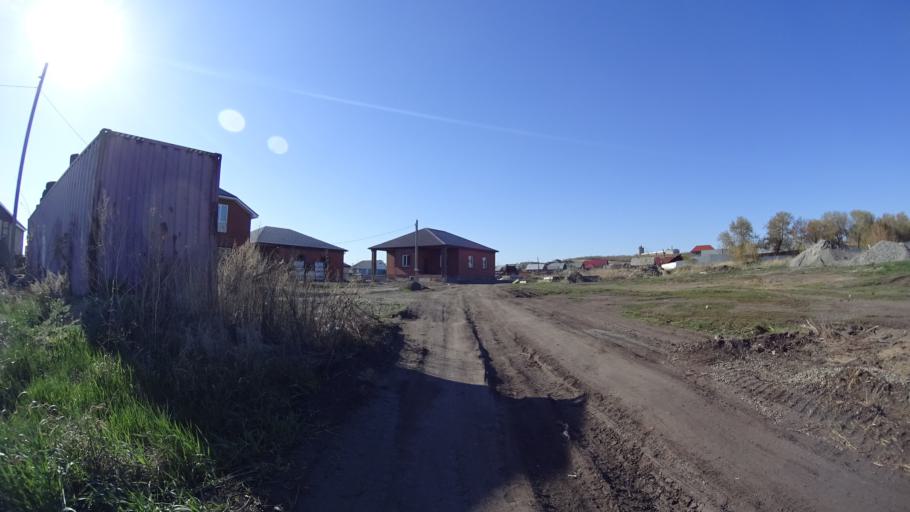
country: RU
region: Chelyabinsk
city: Troitsk
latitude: 54.0948
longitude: 61.5989
